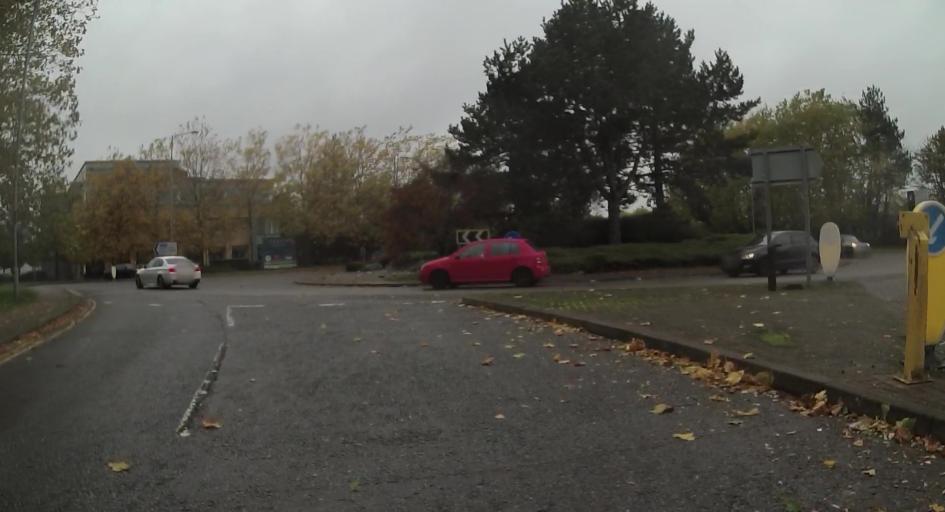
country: GB
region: England
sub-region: Surrey
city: Byfleet
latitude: 51.3474
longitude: -0.4719
